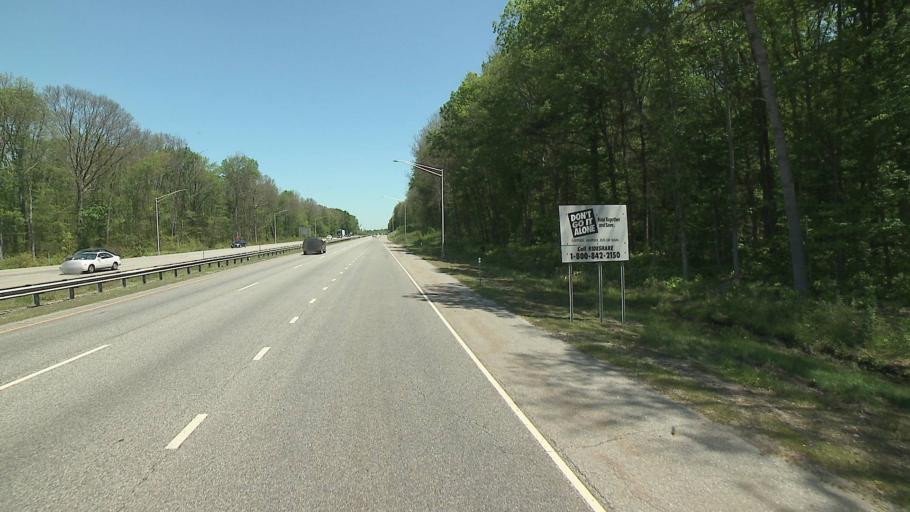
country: US
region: Connecticut
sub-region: Windham County
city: Moosup
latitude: 41.7215
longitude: -71.8933
